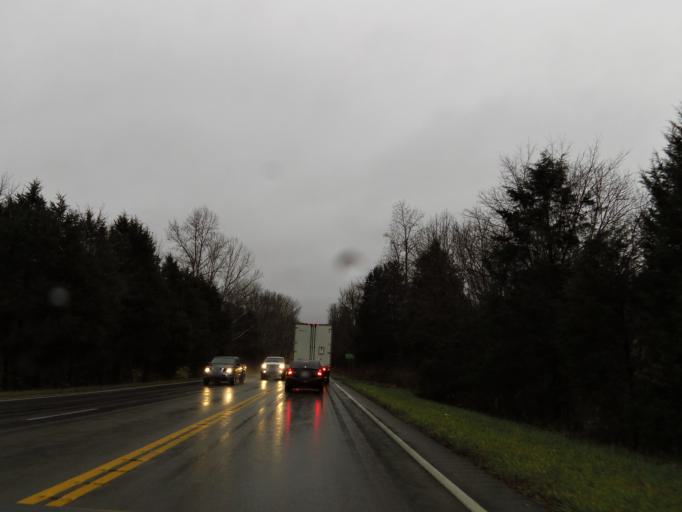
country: US
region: Kentucky
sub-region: Rockcastle County
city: Mount Vernon
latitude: 37.3995
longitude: -84.3346
